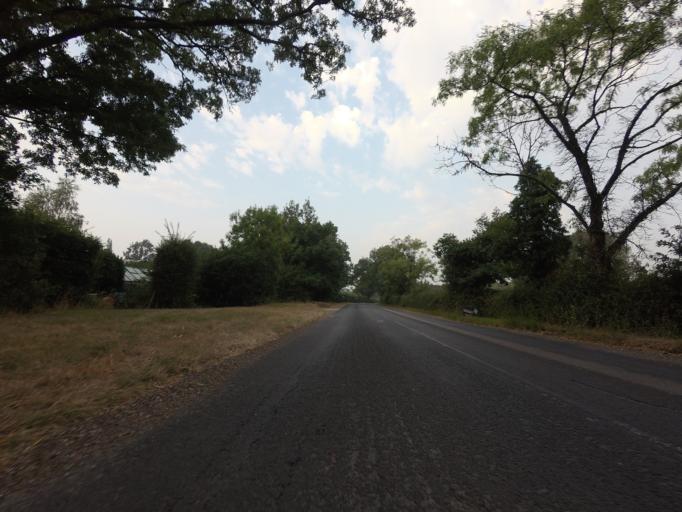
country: GB
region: England
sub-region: Kent
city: Lenham
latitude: 51.1657
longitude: 0.7363
